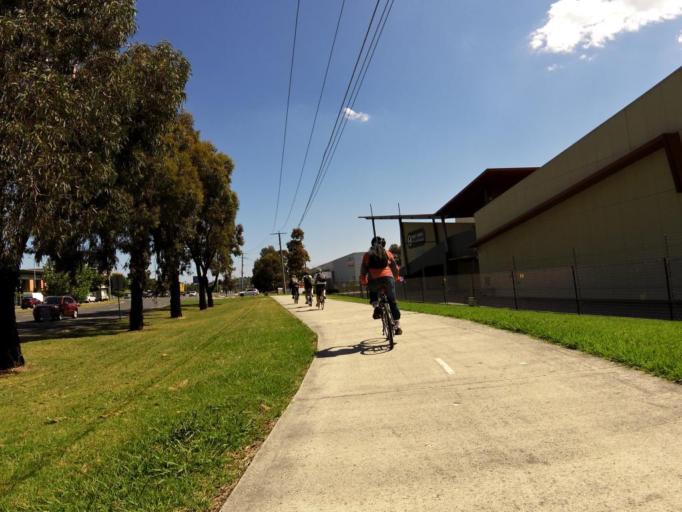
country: AU
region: Victoria
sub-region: Knox
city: Scoresby
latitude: -37.8998
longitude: 145.2205
